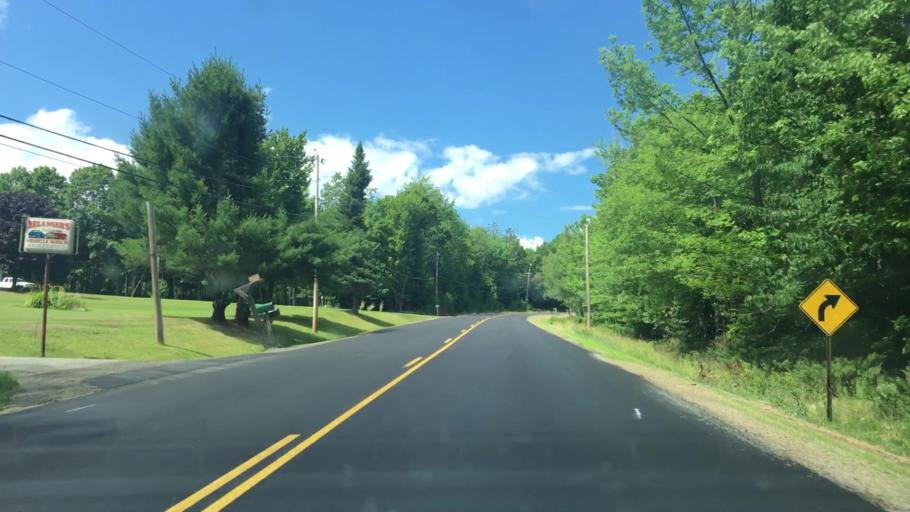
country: US
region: Maine
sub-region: Franklin County
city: Jay
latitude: 44.5461
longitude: -70.1890
